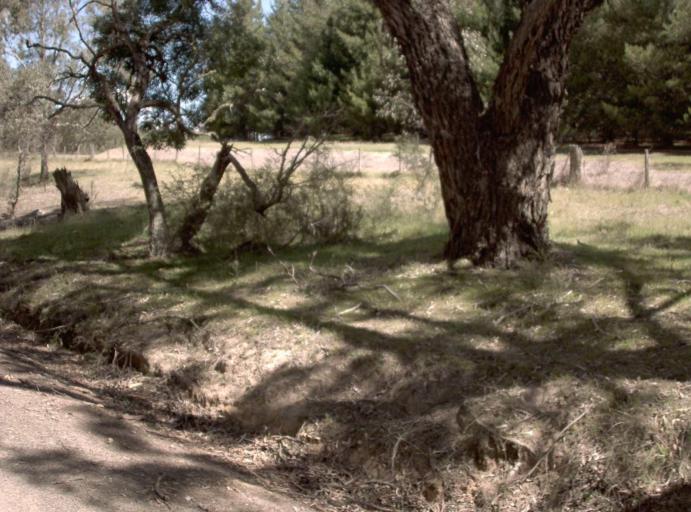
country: AU
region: New South Wales
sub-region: Bombala
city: Bombala
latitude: -37.1233
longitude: 148.6625
